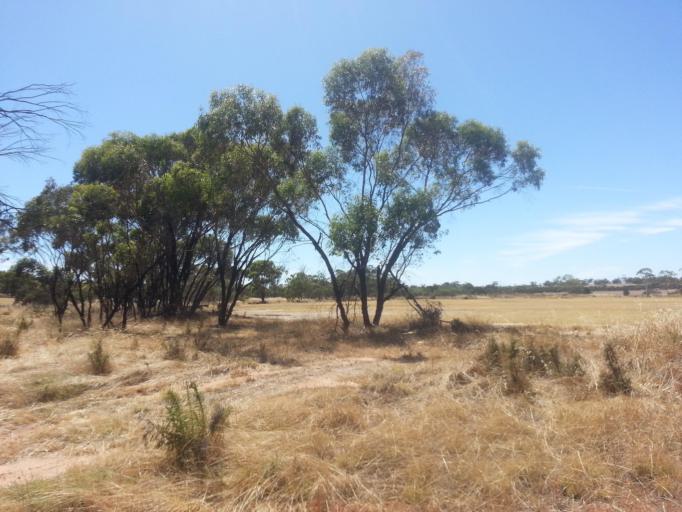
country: AU
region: Western Australia
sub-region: Moora
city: Moora
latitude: -30.2940
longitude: 116.0622
